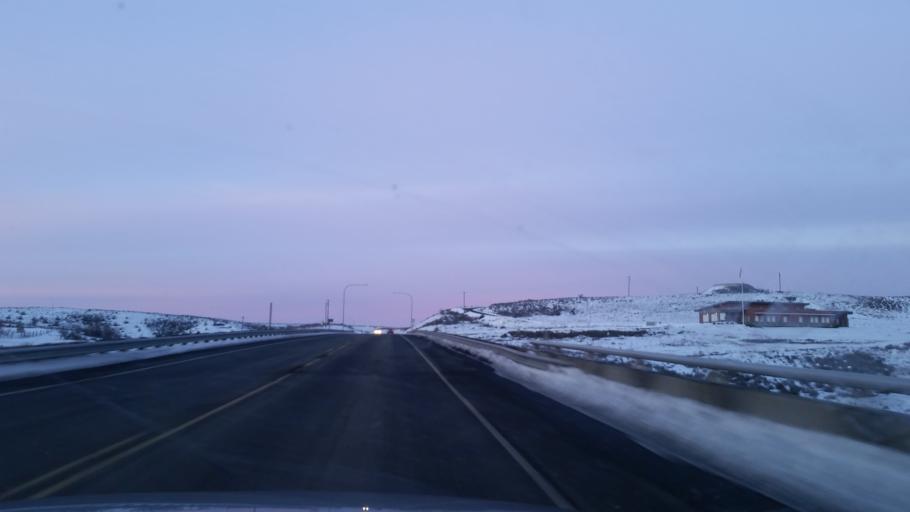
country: US
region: Washington
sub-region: Lincoln County
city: Davenport
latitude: 47.3013
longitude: -117.9733
